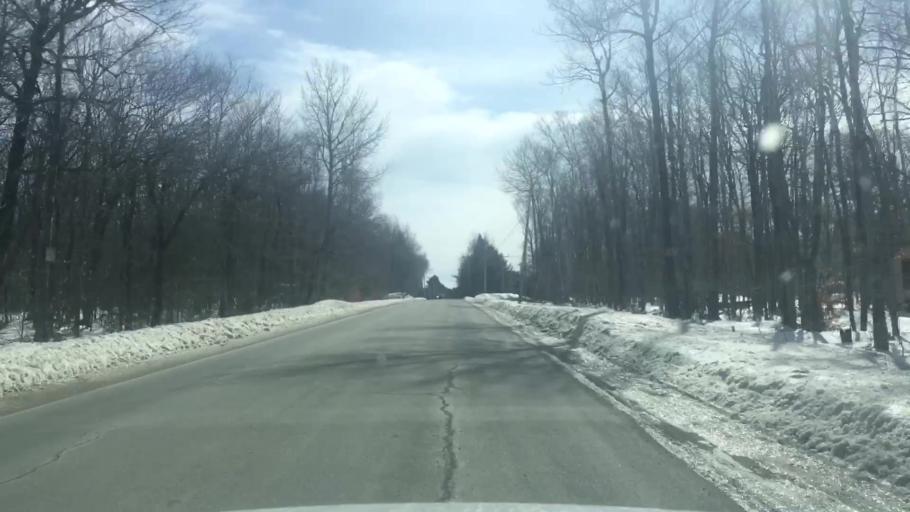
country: US
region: Maine
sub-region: Penobscot County
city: Holden
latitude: 44.7714
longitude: -68.6491
